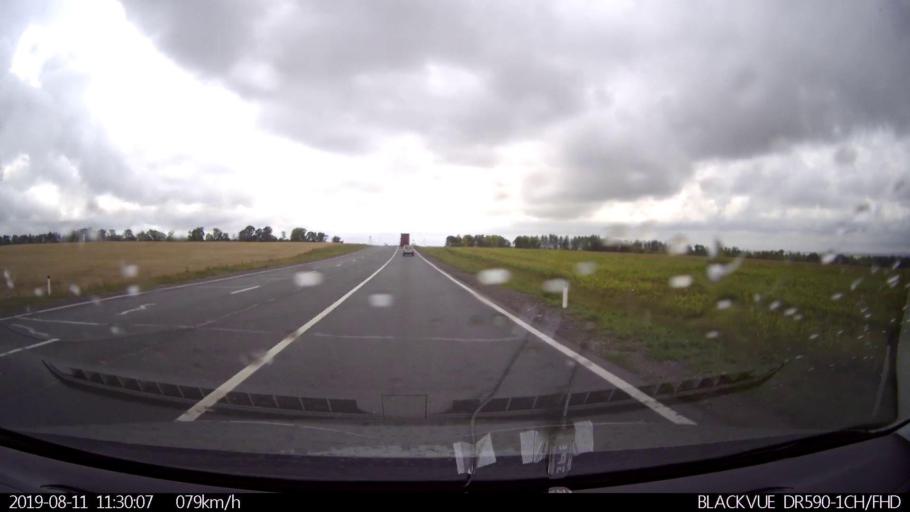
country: RU
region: Ulyanovsk
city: Krasnyy Gulyay
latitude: 54.0620
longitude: 48.2204
